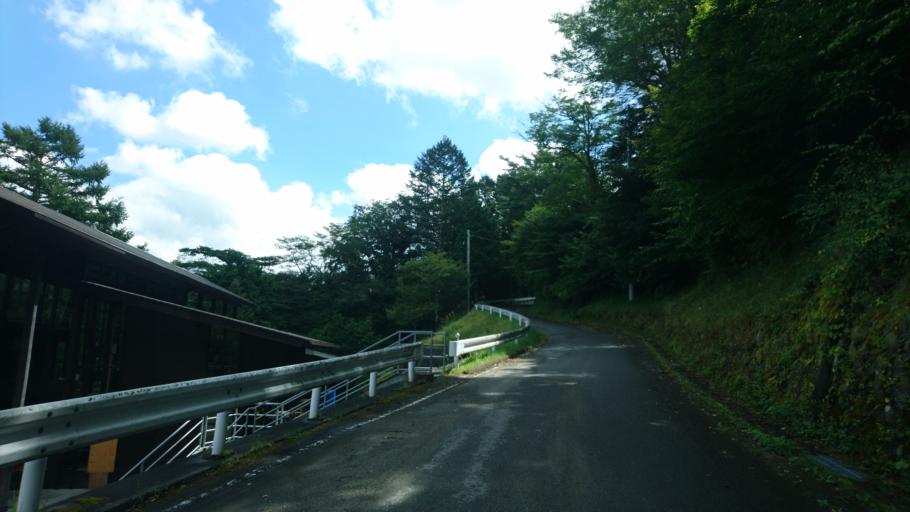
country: JP
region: Gunma
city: Omamacho-omama
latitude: 36.6041
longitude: 139.2388
